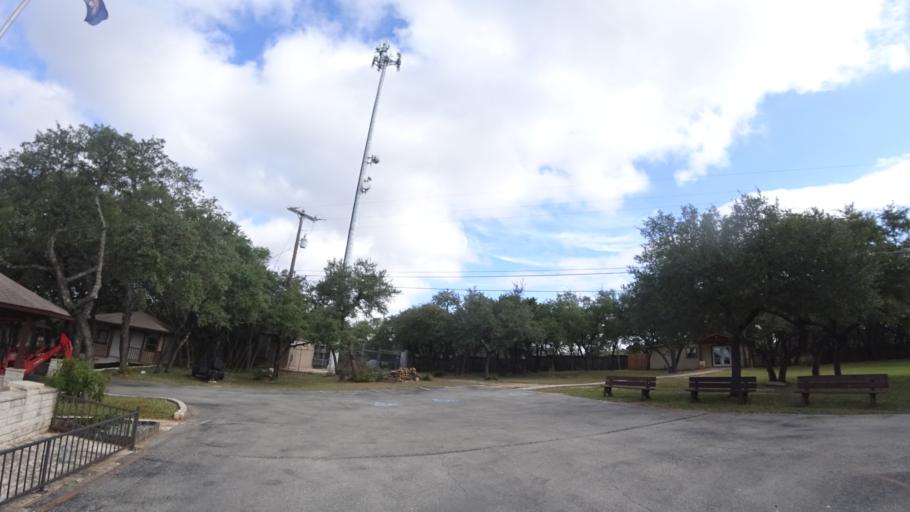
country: US
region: Texas
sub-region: Travis County
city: Bee Cave
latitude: 30.2505
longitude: -97.9236
